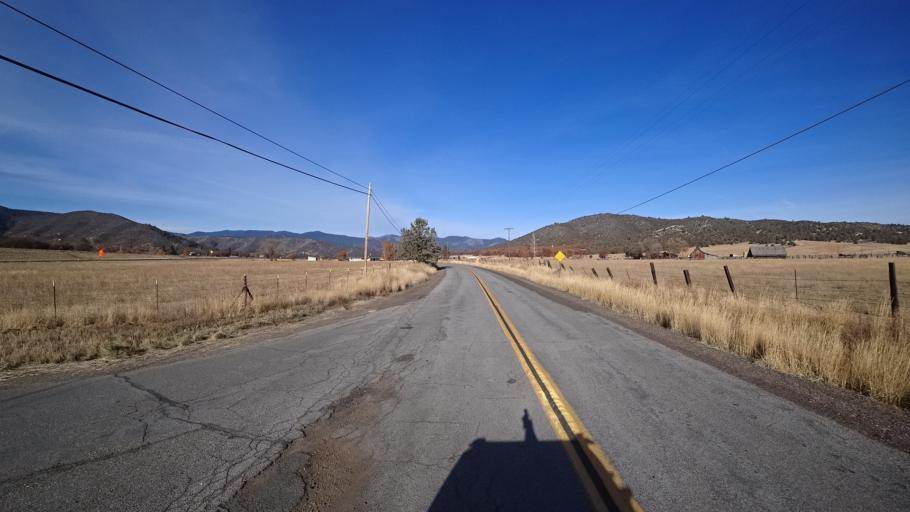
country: US
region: California
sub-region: Siskiyou County
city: Yreka
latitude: 41.6692
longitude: -122.6093
